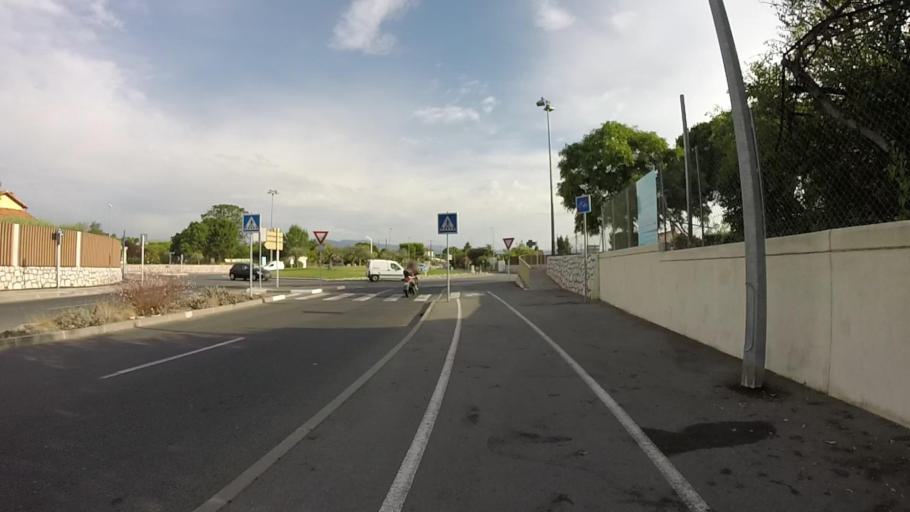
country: FR
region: Provence-Alpes-Cote d'Azur
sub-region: Departement des Alpes-Maritimes
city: Biot
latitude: 43.6026
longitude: 7.1128
